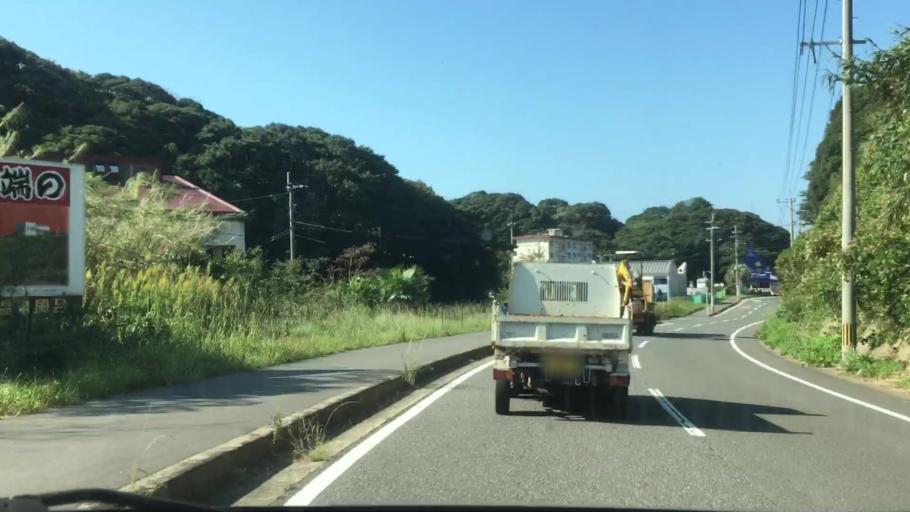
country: JP
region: Nagasaki
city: Sasebo
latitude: 33.0248
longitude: 129.5771
